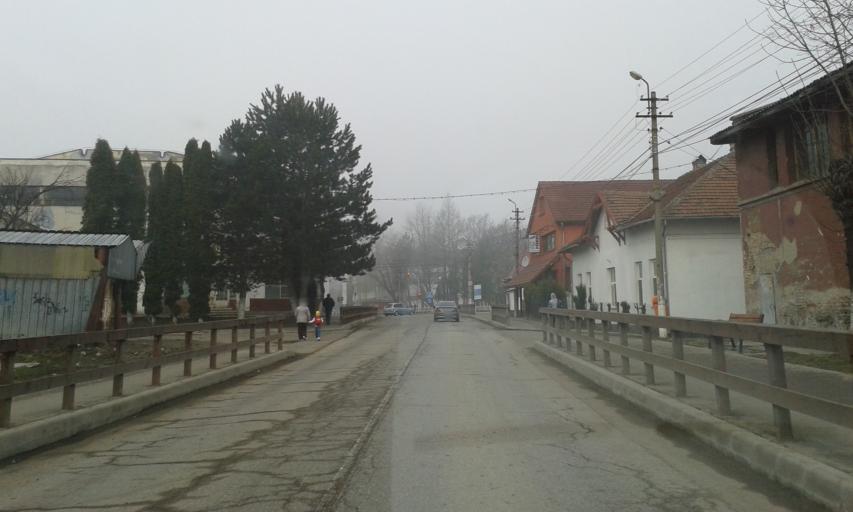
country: RO
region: Hunedoara
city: Vulcan
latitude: 45.3766
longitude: 23.2964
